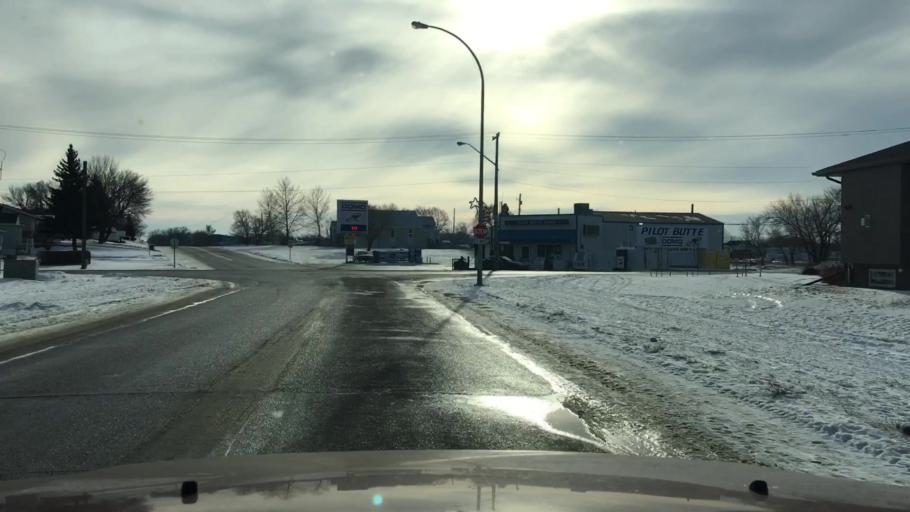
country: CA
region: Saskatchewan
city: Pilot Butte
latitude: 50.4848
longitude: -104.4202
